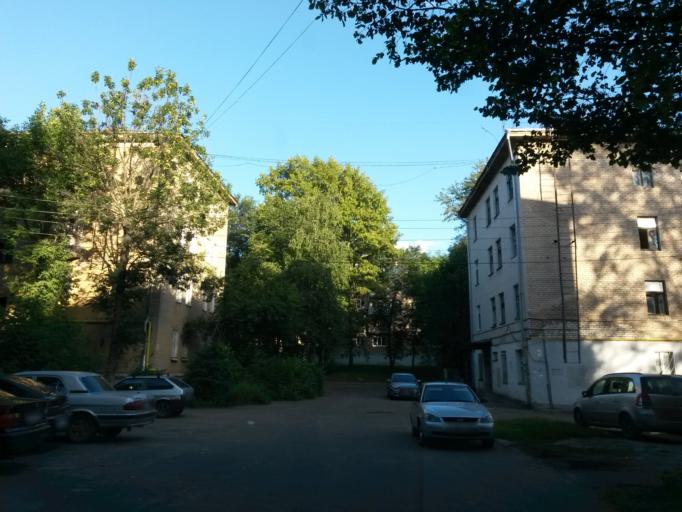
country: RU
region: Jaroslavl
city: Yaroslavl
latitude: 57.5802
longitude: 39.8446
